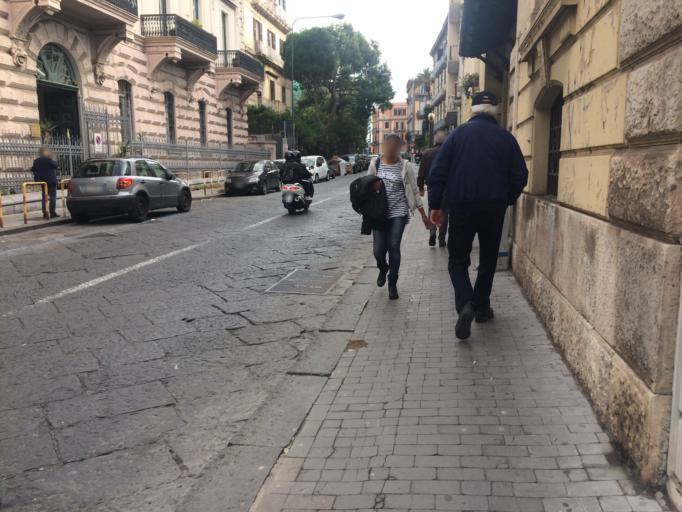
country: IT
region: Campania
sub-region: Provincia di Napoli
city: Napoli
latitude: 40.8355
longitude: 14.2267
